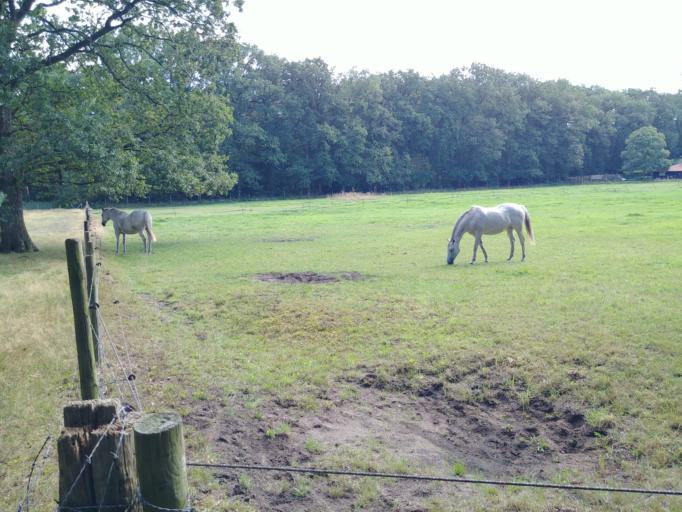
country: NL
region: Utrecht
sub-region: Gemeente Utrechtse Heuvelrug
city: Maarn
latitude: 52.0588
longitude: 5.3696
